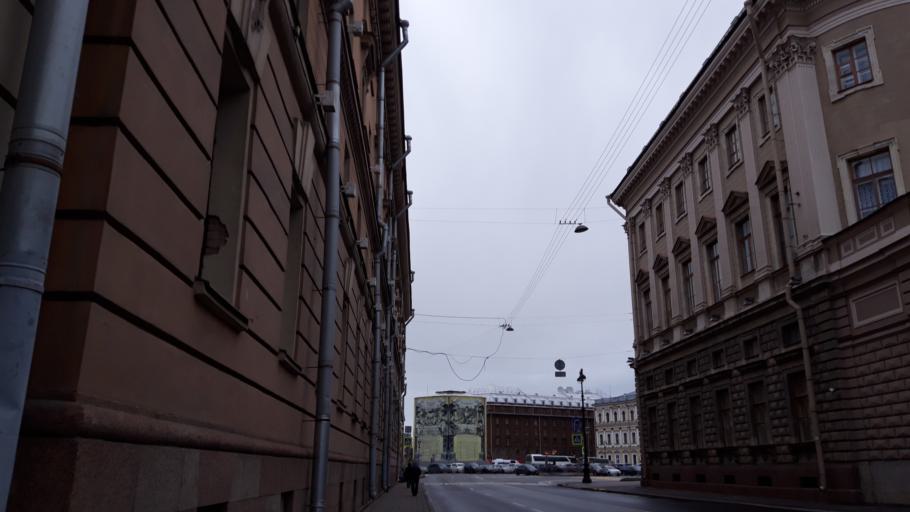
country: RU
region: St.-Petersburg
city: Saint Petersburg
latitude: 59.9303
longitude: 30.3083
